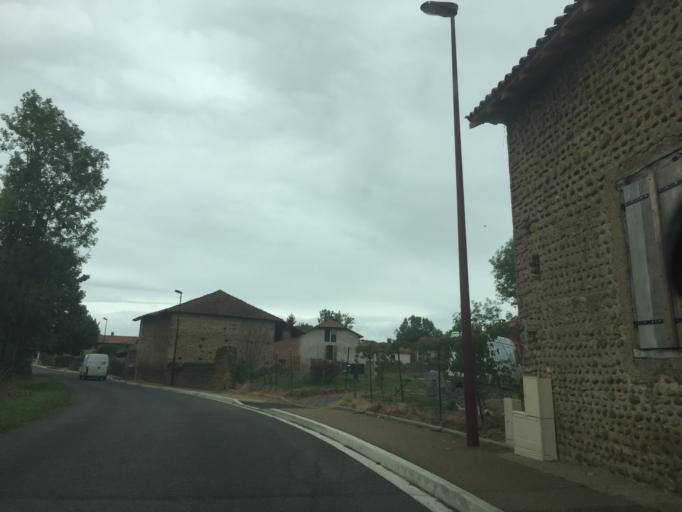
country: FR
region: Midi-Pyrenees
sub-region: Departement des Hautes-Pyrenees
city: Rabastens-de-Bigorre
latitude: 43.3308
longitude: 0.2281
